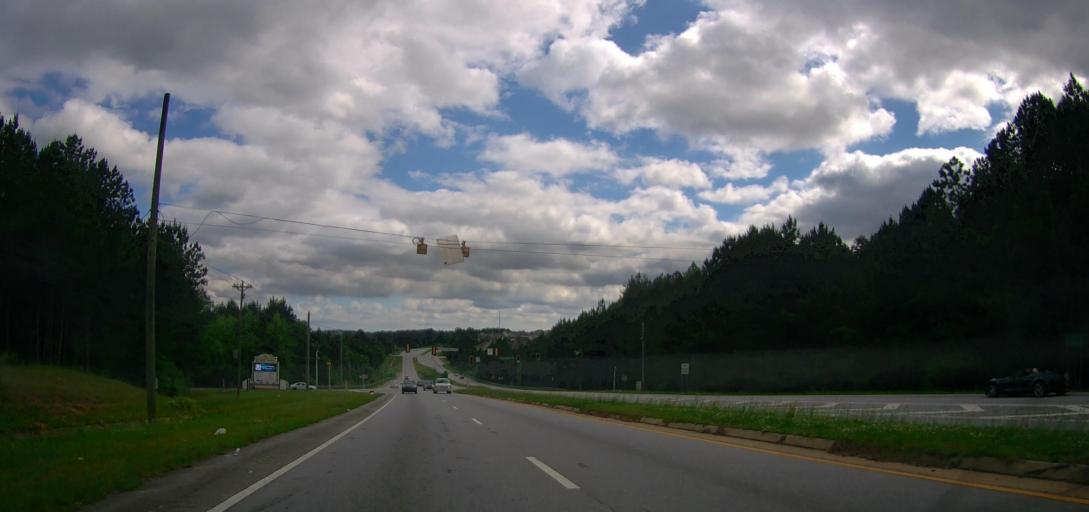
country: US
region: Georgia
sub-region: Rockdale County
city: Conyers
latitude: 33.6902
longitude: -83.9617
